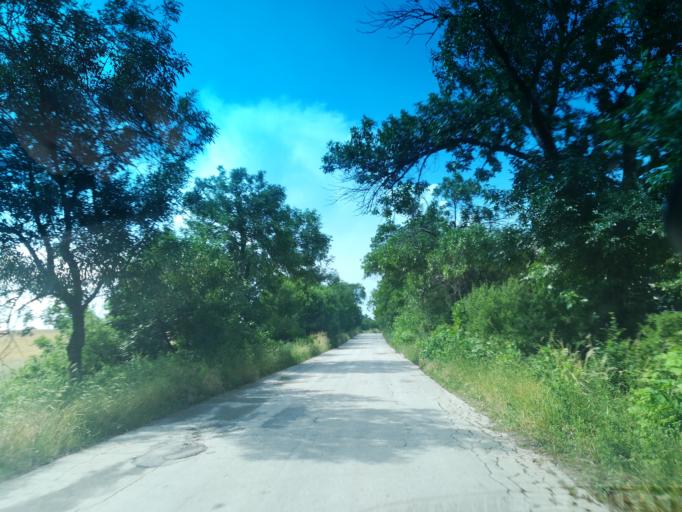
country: BG
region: Khaskovo
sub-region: Obshtina Mineralni Bani
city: Mineralni Bani
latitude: 42.0007
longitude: 25.2246
